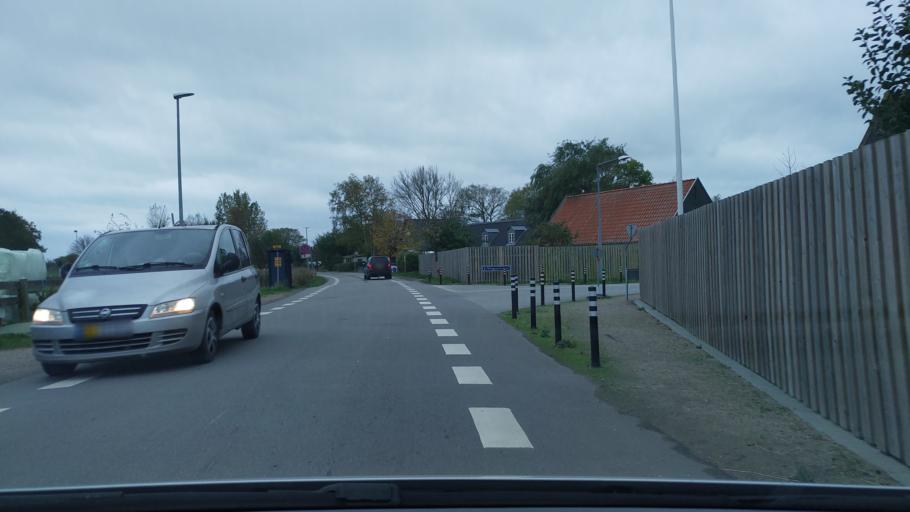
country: DK
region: Capital Region
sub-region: Tarnby Kommune
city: Tarnby
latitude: 55.5931
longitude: 12.5969
